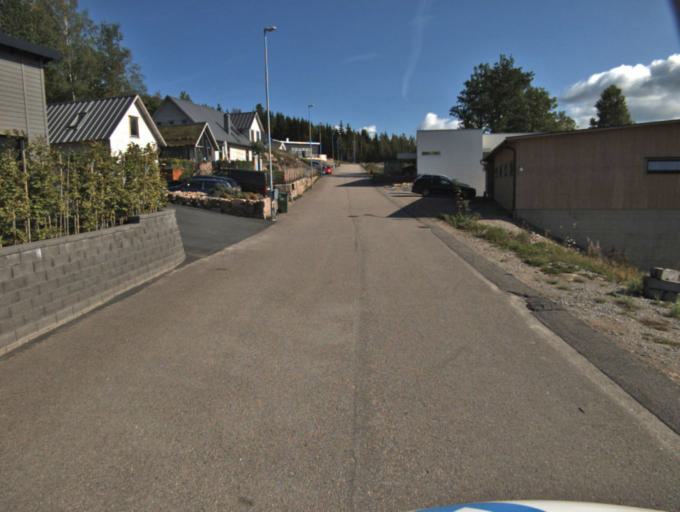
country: SE
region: Vaestra Goetaland
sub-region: Ulricehamns Kommun
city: Ulricehamn
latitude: 57.8058
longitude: 13.3976
